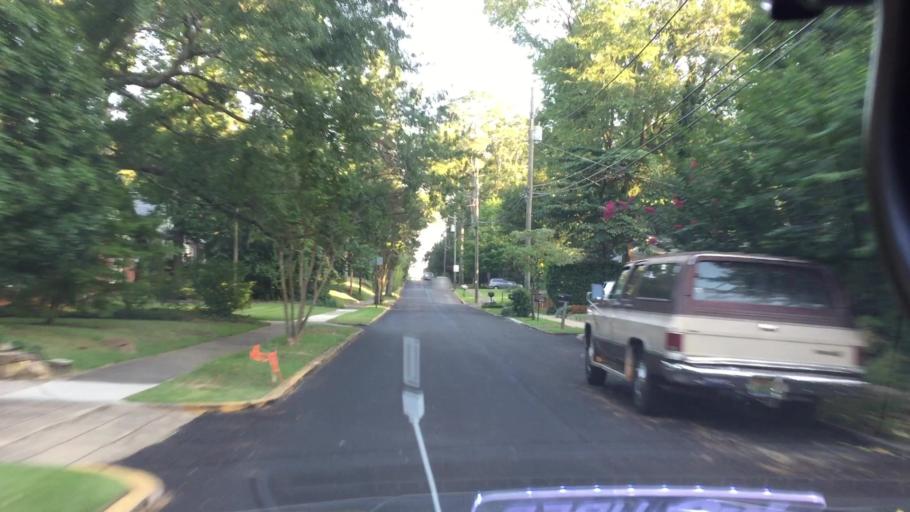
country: US
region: Alabama
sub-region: Lee County
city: Auburn
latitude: 32.6025
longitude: -85.4763
